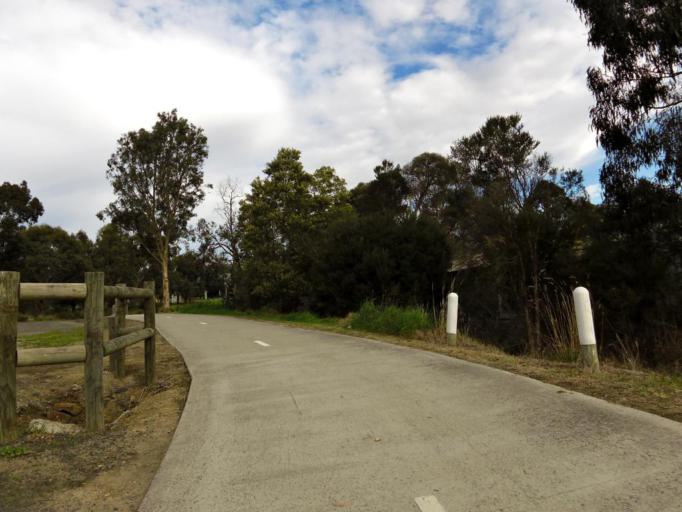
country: AU
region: Victoria
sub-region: Knox
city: Wantirna
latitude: -37.8578
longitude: 145.2084
